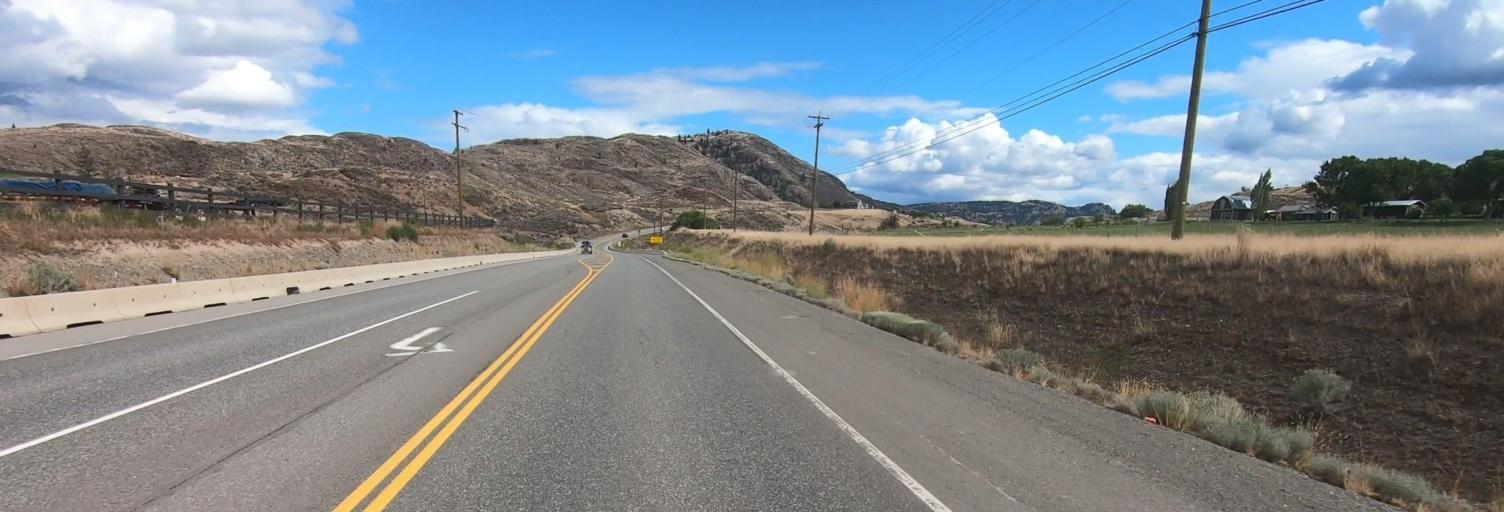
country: CA
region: British Columbia
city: Logan Lake
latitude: 50.7174
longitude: -120.6392
